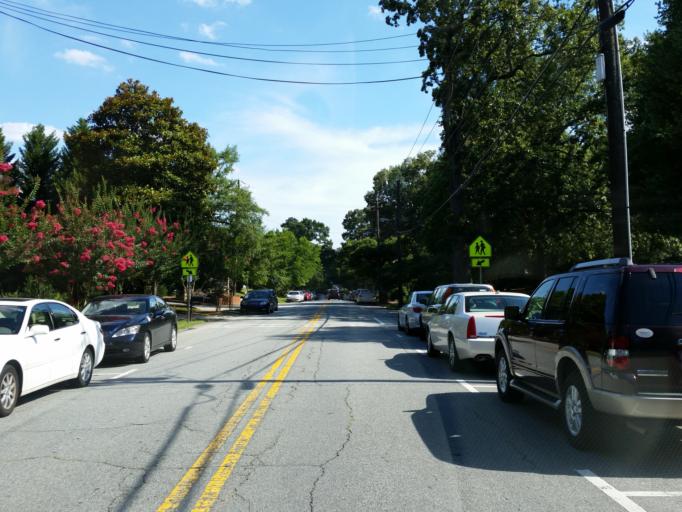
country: US
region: Georgia
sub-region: Fulton County
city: Roswell
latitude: 34.0209
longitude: -84.3634
